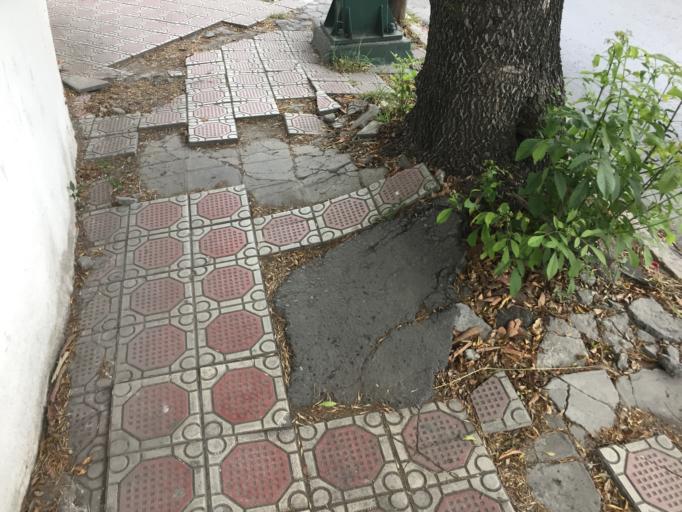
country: MX
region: Nuevo Leon
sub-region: Monterrey
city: Monterrey
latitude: 25.6798
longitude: -100.3072
